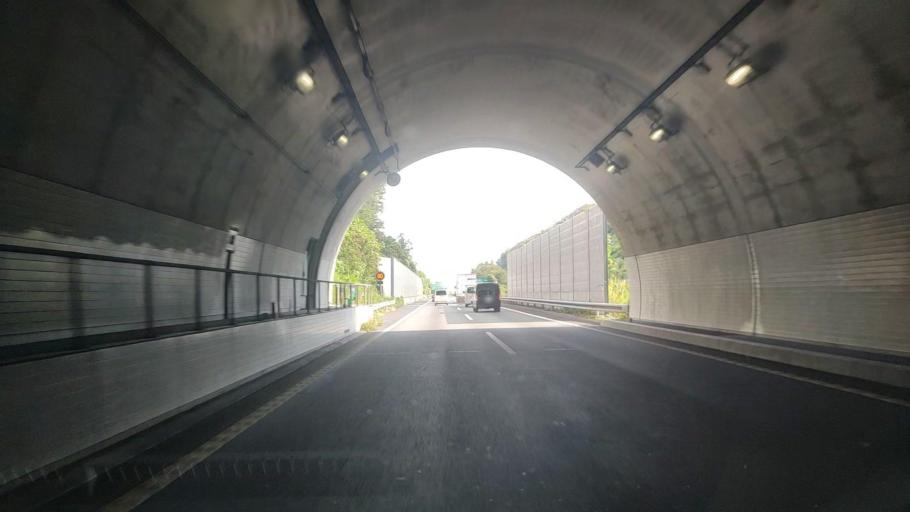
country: JP
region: Tokyo
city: Hachioji
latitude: 35.5600
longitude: 139.3124
